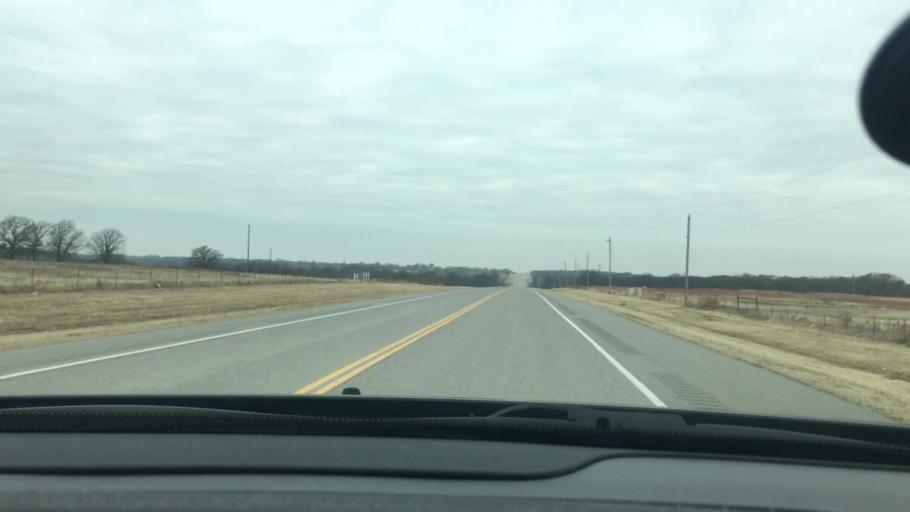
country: US
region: Oklahoma
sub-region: Garvin County
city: Wynnewood
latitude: 34.4925
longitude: -97.3944
